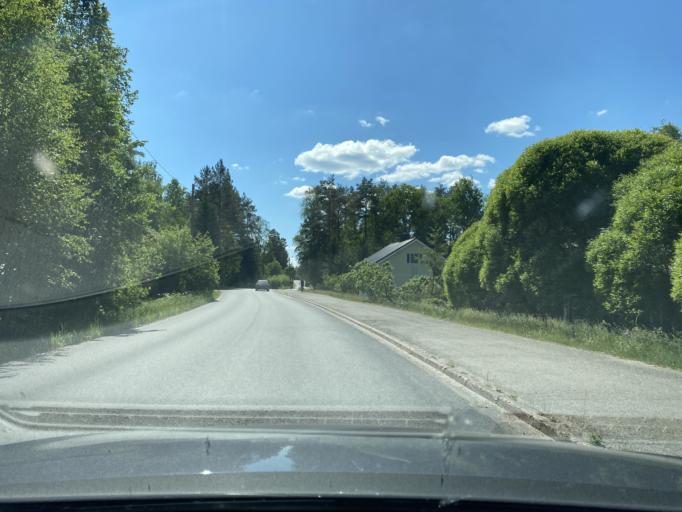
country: FI
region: Satakunta
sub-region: Rauma
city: Eura
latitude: 61.1283
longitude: 22.1637
